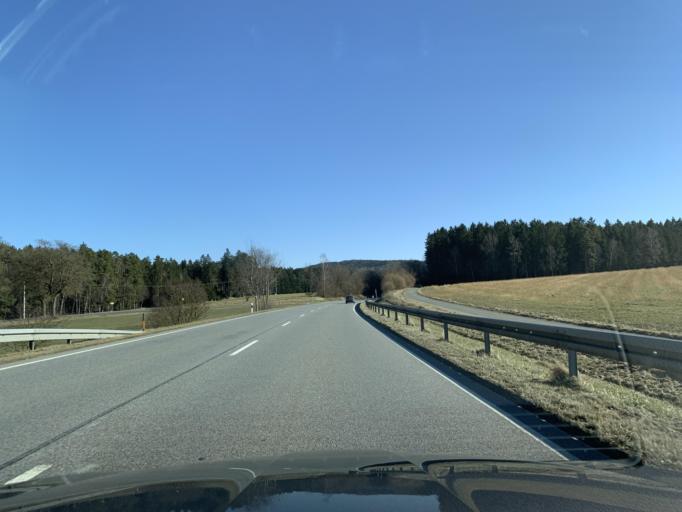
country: DE
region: Bavaria
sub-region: Upper Palatinate
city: Schonthal
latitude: 49.3283
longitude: 12.6299
